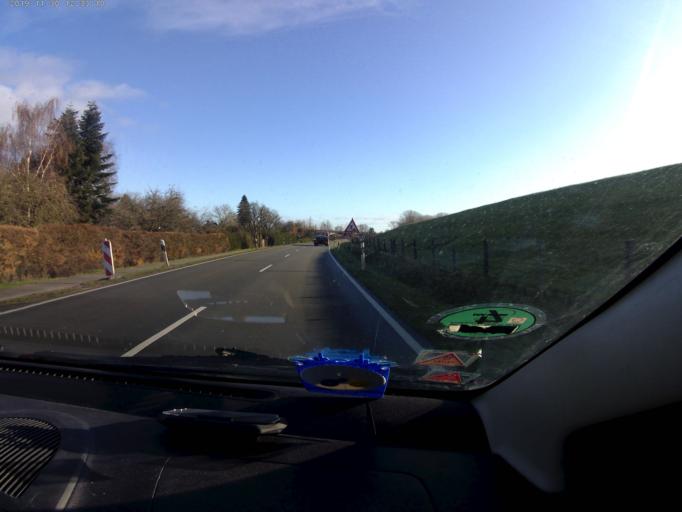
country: DE
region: Lower Saxony
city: Leer
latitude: 53.2329
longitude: 7.4220
